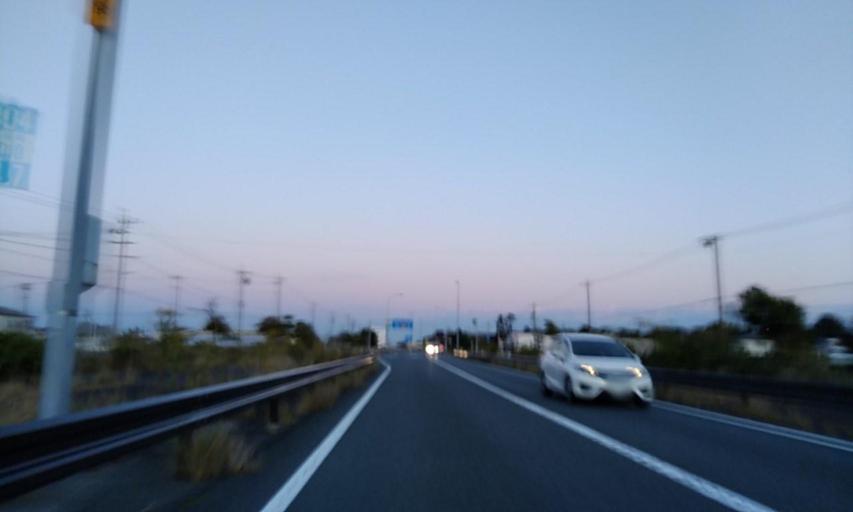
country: JP
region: Shizuoka
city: Hamamatsu
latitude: 34.6809
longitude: 137.6595
